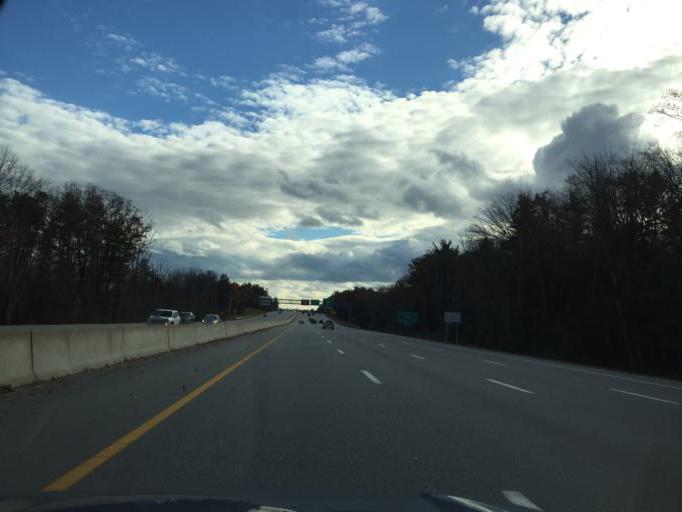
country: US
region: New Hampshire
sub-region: Hillsborough County
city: Bedford
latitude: 42.9315
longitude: -71.4682
